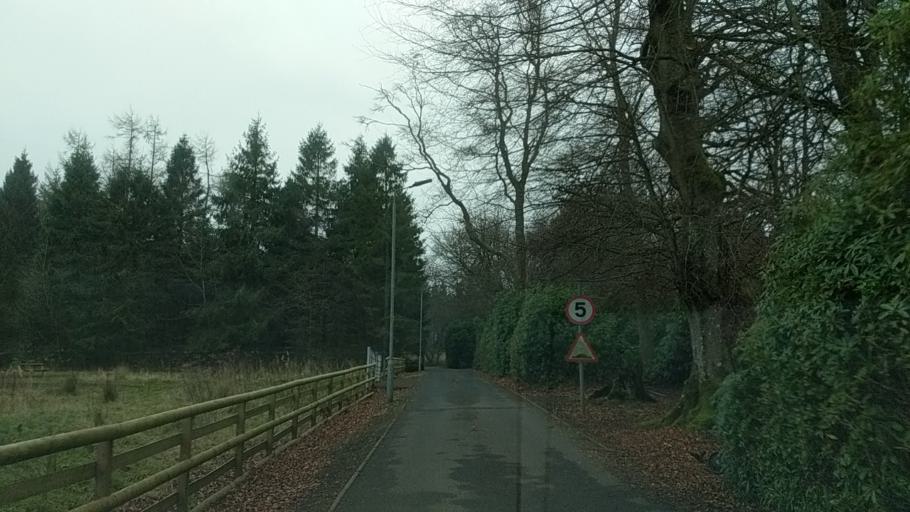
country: GB
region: Scotland
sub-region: South Lanarkshire
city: East Kilbride
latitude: 55.7481
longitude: -4.1487
